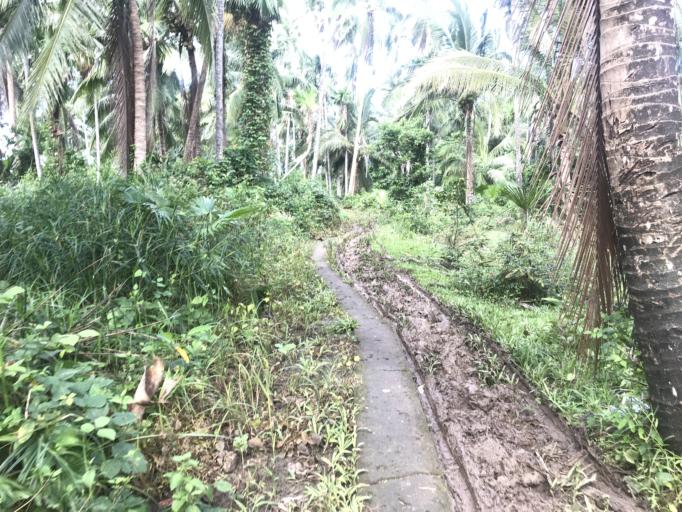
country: PH
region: Calabarzon
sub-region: Province of Quezon
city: Macalelon
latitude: 13.7817
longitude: 122.1417
